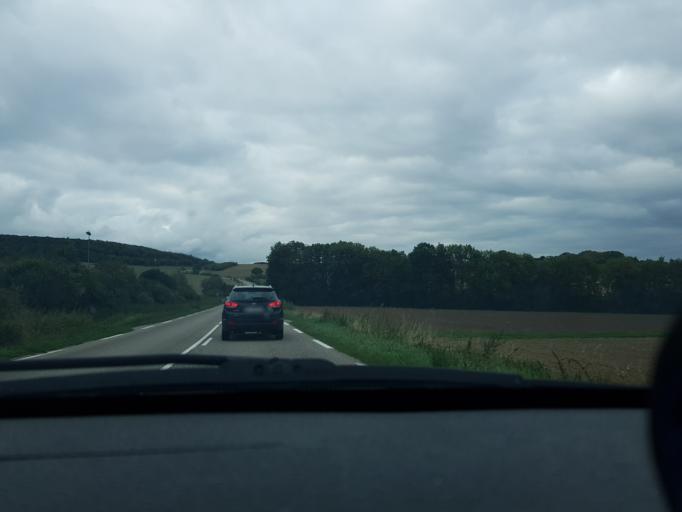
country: FR
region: Lorraine
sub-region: Departement de la Moselle
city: Chateau-Salins
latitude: 48.8753
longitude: 6.5348
